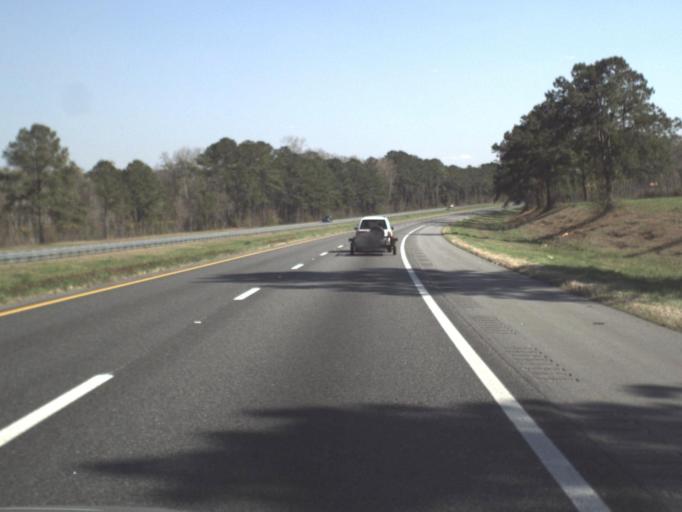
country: US
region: Florida
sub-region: Gadsden County
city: Gretna
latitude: 30.6021
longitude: -84.7306
